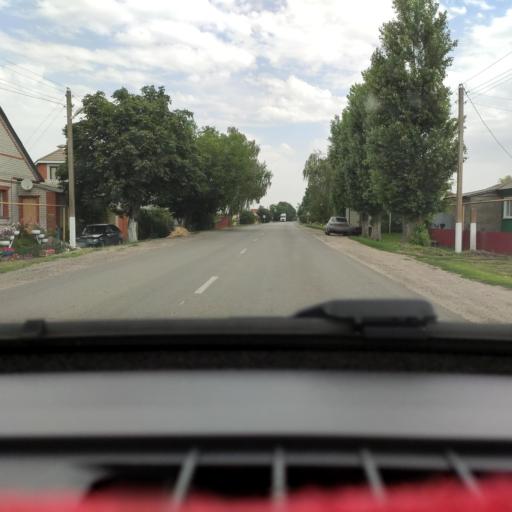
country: RU
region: Voronezj
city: Davydovka
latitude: 51.2013
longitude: 39.5077
